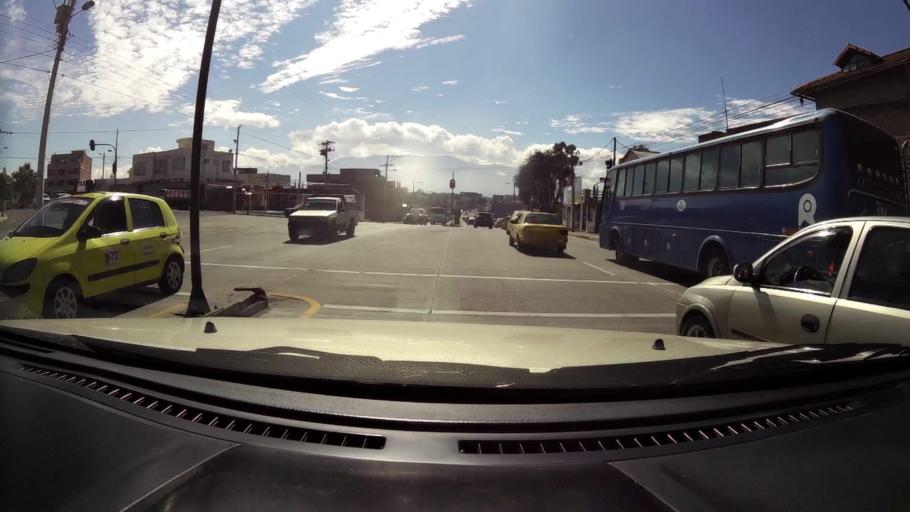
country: EC
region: Chimborazo
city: Riobamba
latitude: -1.6631
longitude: -78.6713
